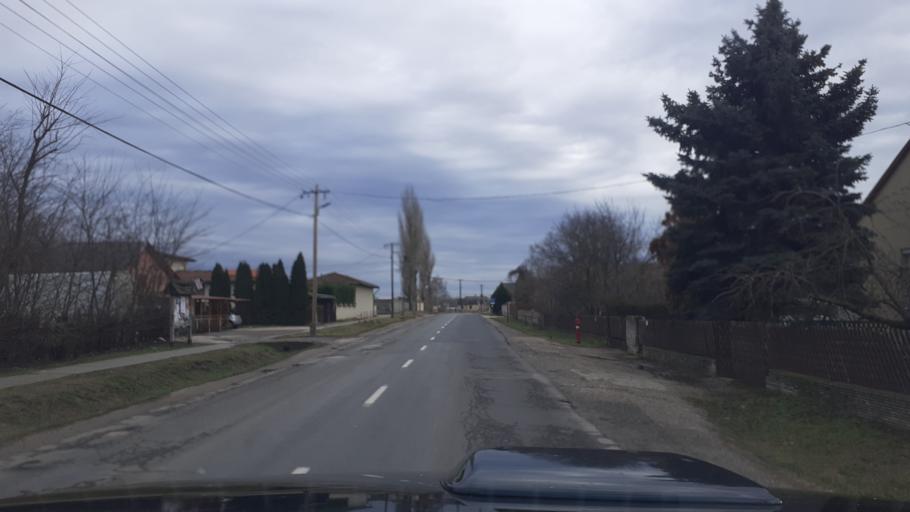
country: HU
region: Fejer
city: Sarosd
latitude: 47.0386
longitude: 18.6547
